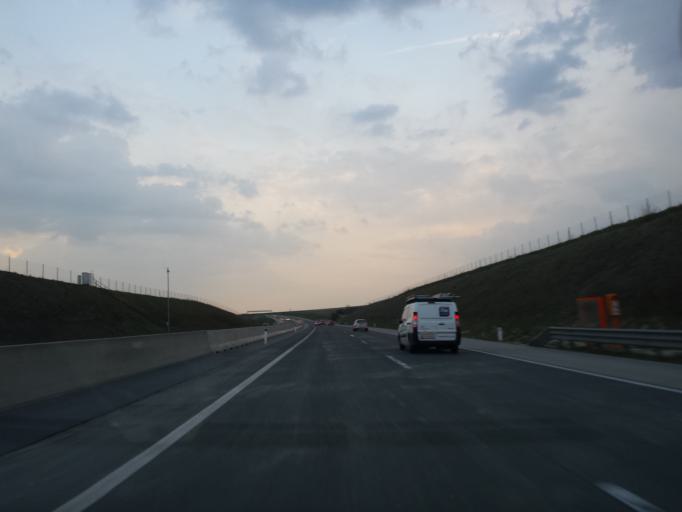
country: AT
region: Lower Austria
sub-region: Politischer Bezirk Mistelbach
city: Hochleithen
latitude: 48.4675
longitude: 16.5562
